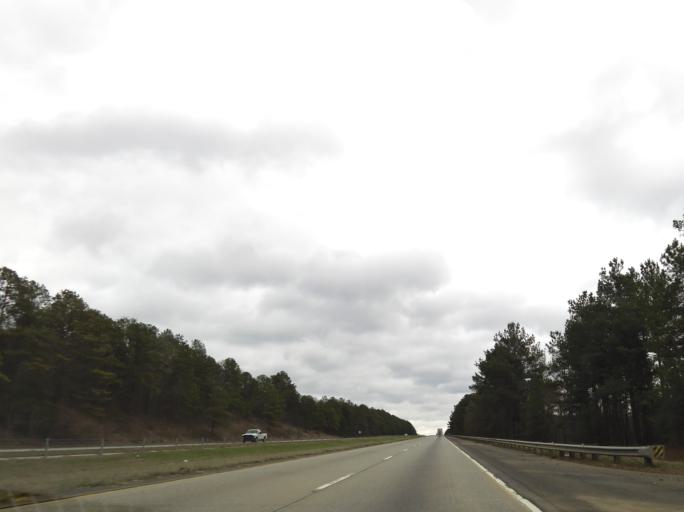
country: US
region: Georgia
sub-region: Twiggs County
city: Jeffersonville
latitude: 32.6718
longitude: -83.4723
